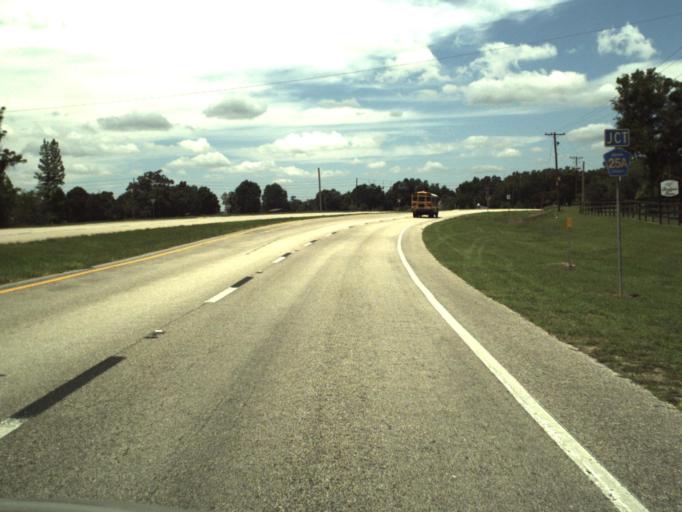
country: US
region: Florida
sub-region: Marion County
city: Citra
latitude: 29.4005
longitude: -82.2054
